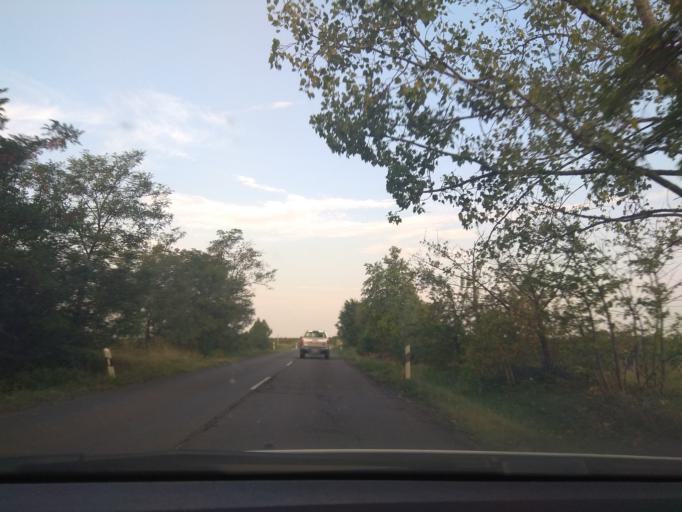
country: HU
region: Heves
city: Andornaktalya
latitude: 47.8334
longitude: 20.4376
